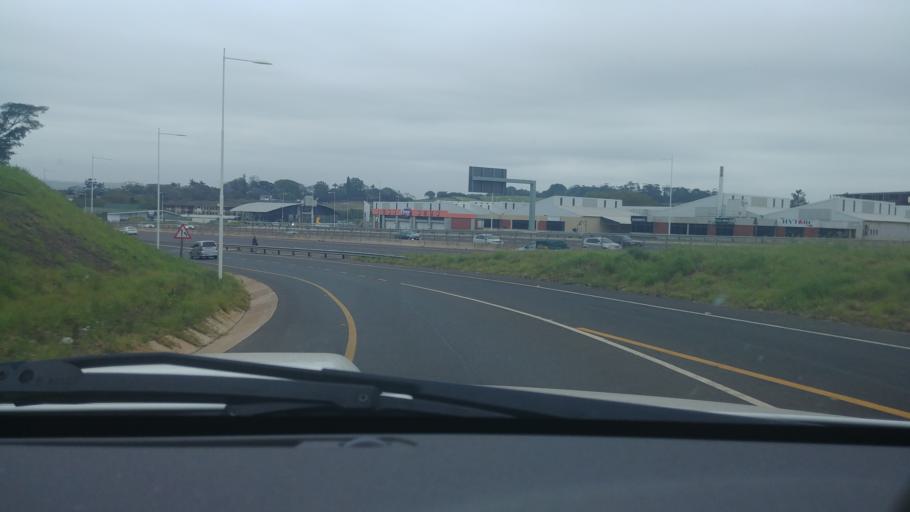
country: ZA
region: KwaZulu-Natal
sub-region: eThekwini Metropolitan Municipality
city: Durban
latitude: -29.7113
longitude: 31.0505
